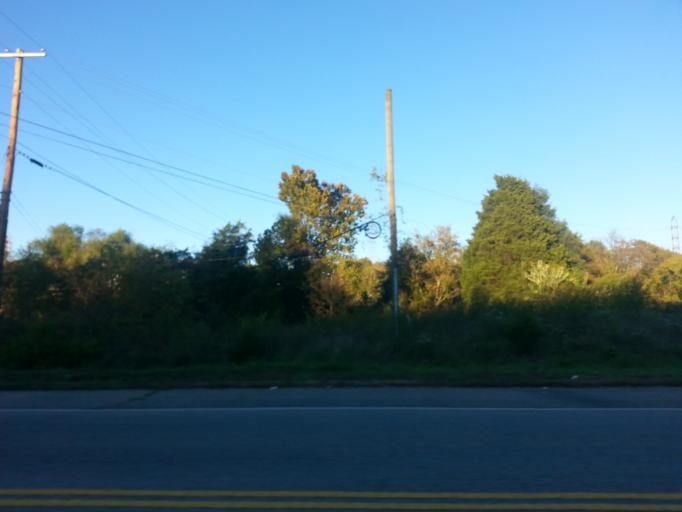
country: US
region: Tennessee
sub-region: Knox County
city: Knoxville
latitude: 36.0254
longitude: -83.9908
